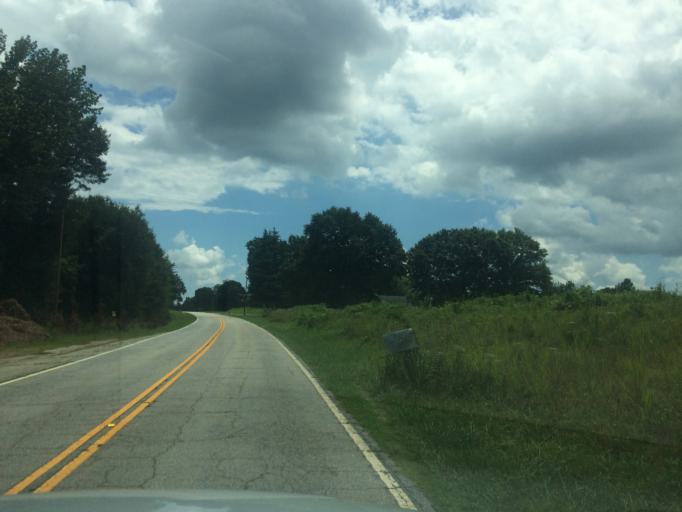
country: US
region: South Carolina
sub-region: Spartanburg County
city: Landrum
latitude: 35.1865
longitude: -82.0460
